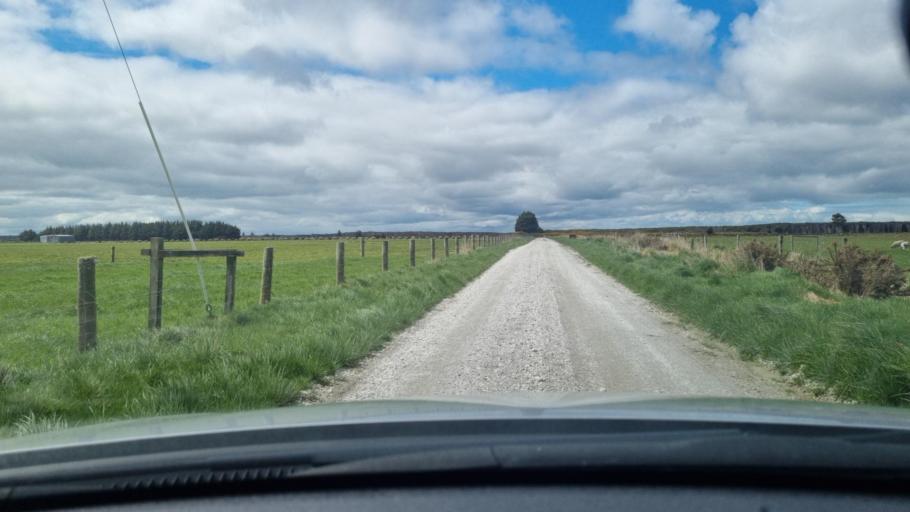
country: NZ
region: Southland
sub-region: Invercargill City
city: Invercargill
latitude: -46.5066
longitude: 168.4408
